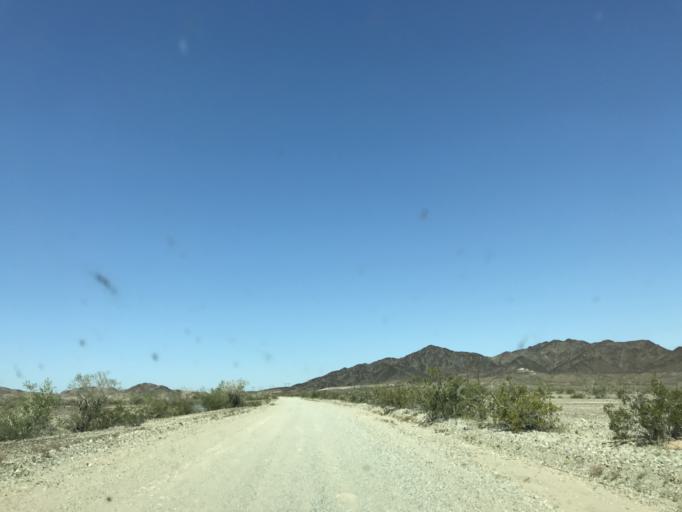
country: US
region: California
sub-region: Riverside County
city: Mesa Verde
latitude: 33.4924
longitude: -114.8117
